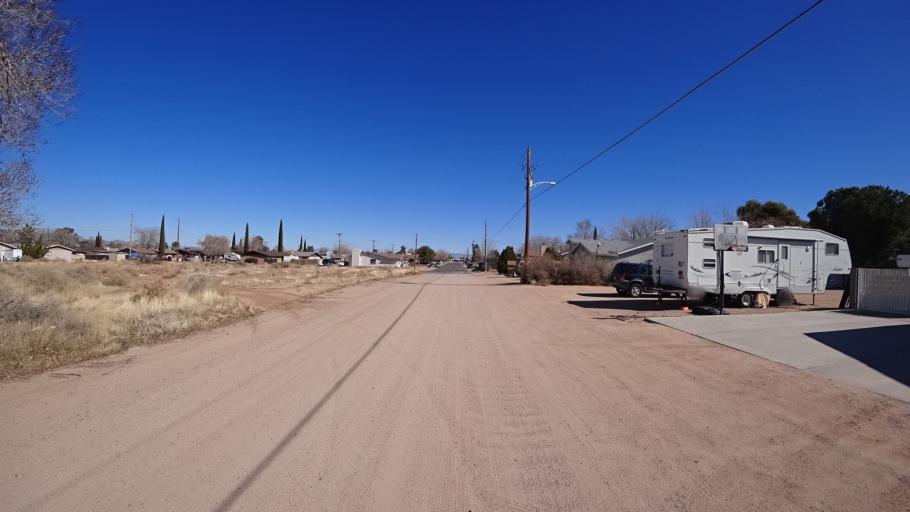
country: US
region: Arizona
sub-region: Mohave County
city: Kingman
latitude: 35.2070
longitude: -114.0231
